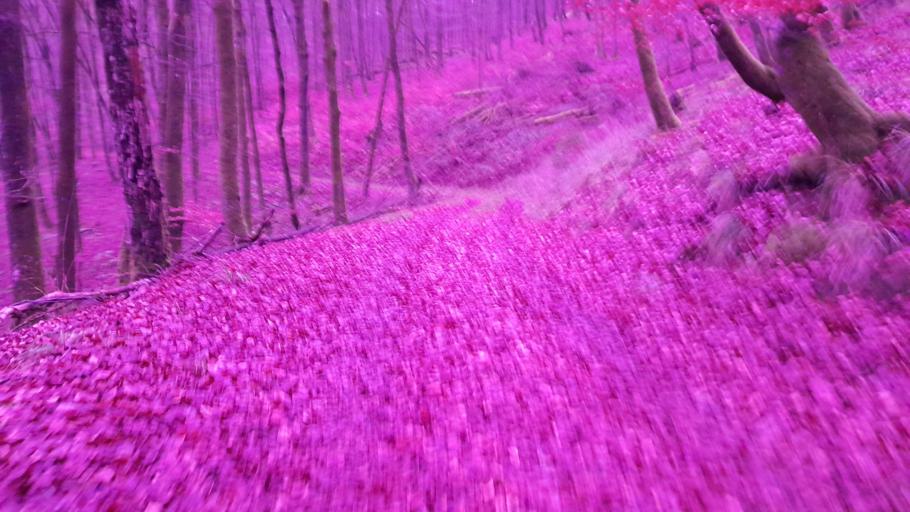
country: DE
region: Rheinland-Pfalz
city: Dasburg
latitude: 50.0732
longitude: 6.1044
